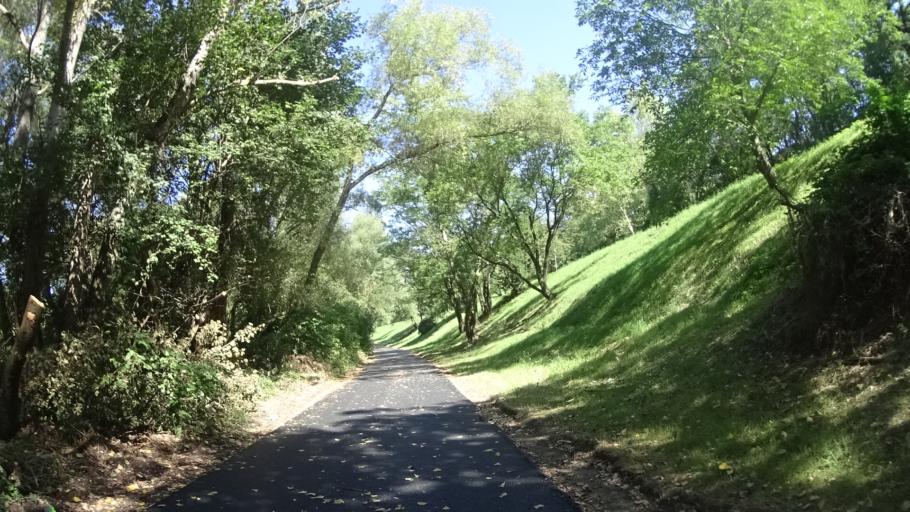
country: AT
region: Lower Austria
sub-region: Politischer Bezirk Bruck an der Leitha
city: Hainburg an der Donau
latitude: 48.1902
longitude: 16.9772
